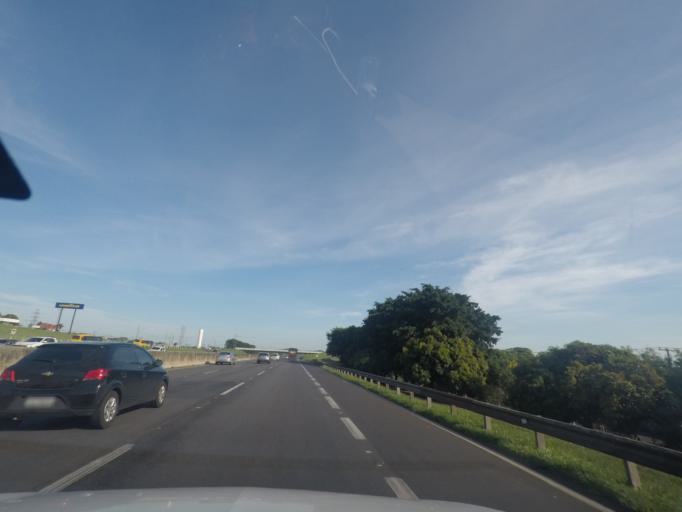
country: BR
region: Sao Paulo
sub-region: Americana
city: Americana
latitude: -22.7033
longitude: -47.3038
